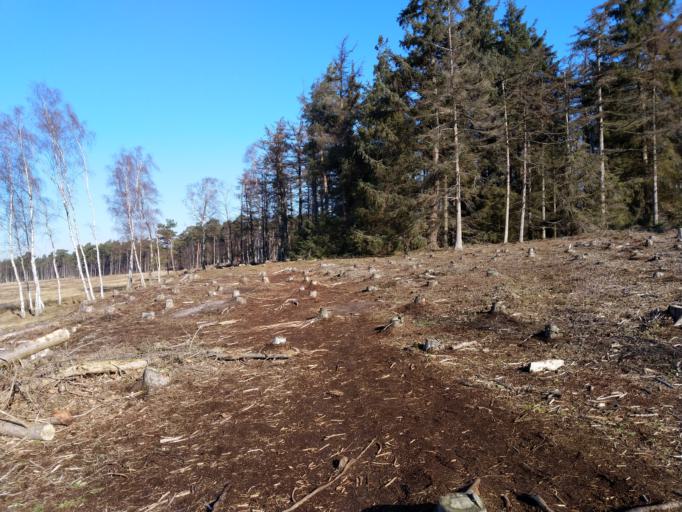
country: DK
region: Zealand
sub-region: Guldborgsund Kommune
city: Nykobing Falster
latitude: 54.6397
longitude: 11.9574
